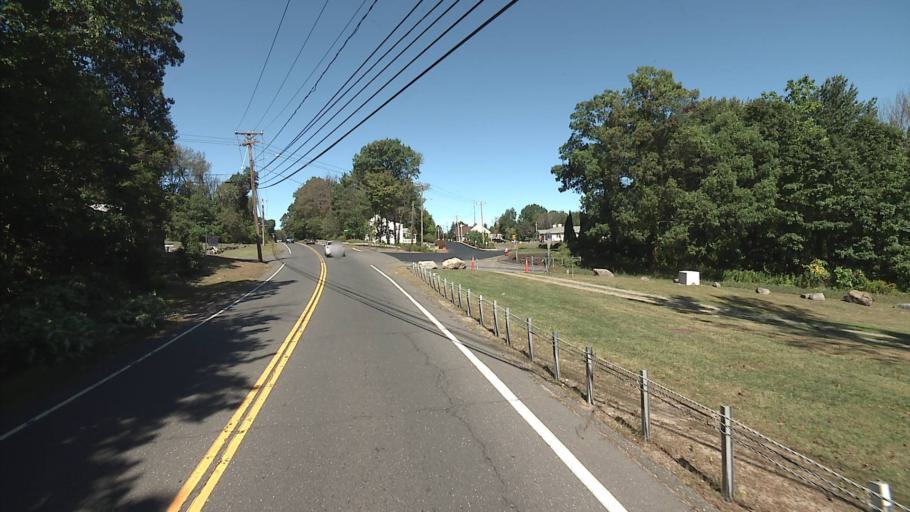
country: US
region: Connecticut
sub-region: New Haven County
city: Prospect
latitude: 41.4980
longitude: -72.9768
